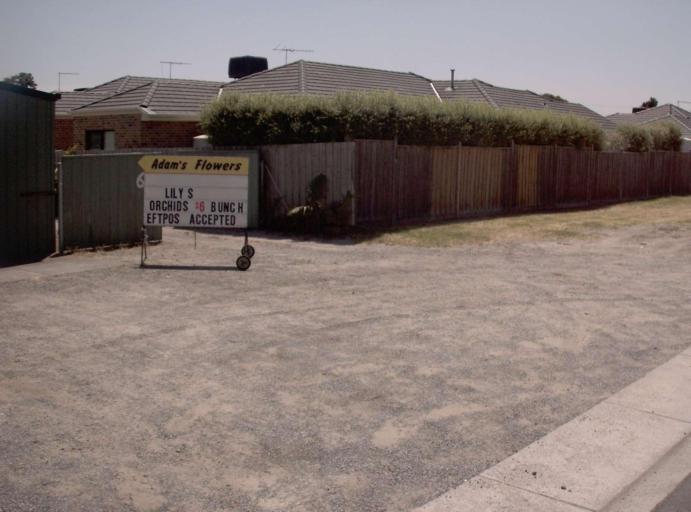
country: AU
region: Victoria
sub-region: Kingston
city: Dingley Village
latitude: -37.9809
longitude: 145.1464
